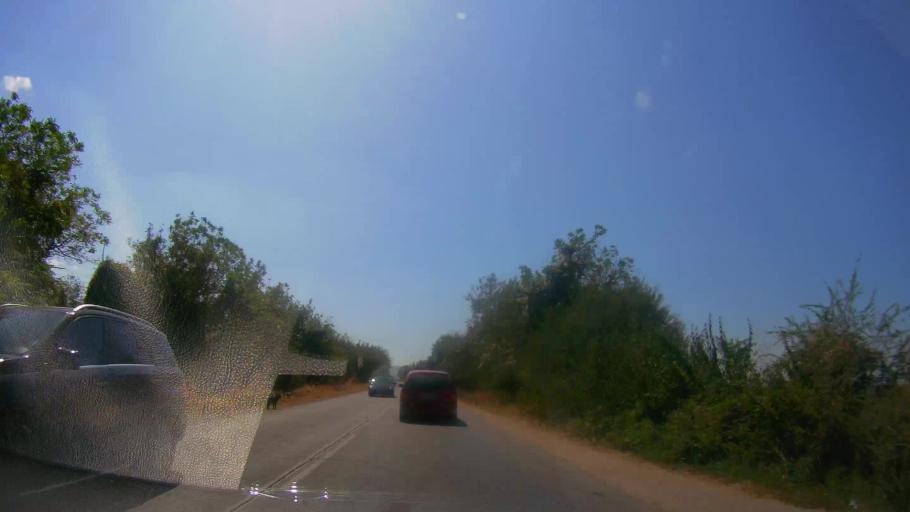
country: BG
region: Veliko Turnovo
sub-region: Obshtina Gorna Oryakhovitsa
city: Purvomaytsi
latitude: 43.2355
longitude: 25.6406
